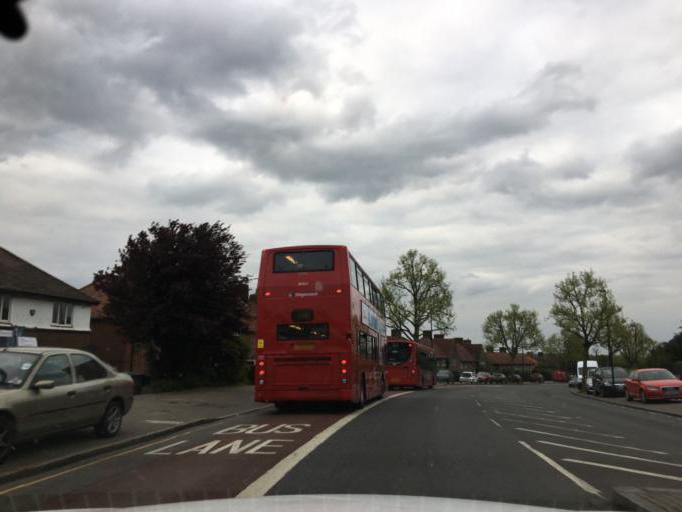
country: GB
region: England
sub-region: Greater London
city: Bromley
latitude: 51.4295
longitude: 0.0140
